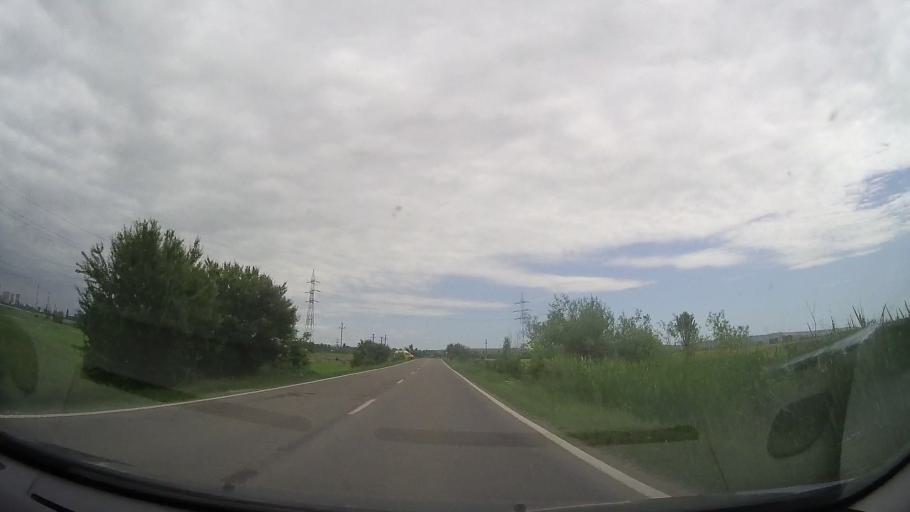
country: RO
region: Prahova
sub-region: Comuna Berceni
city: Berceni
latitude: 44.9298
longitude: 26.1037
